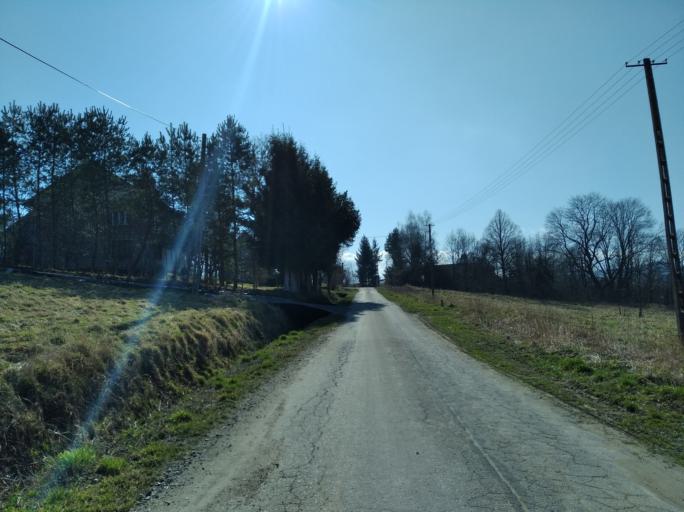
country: PL
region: Subcarpathian Voivodeship
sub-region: Powiat strzyzowski
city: Wysoka Strzyzowska
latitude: 49.8318
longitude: 21.7455
